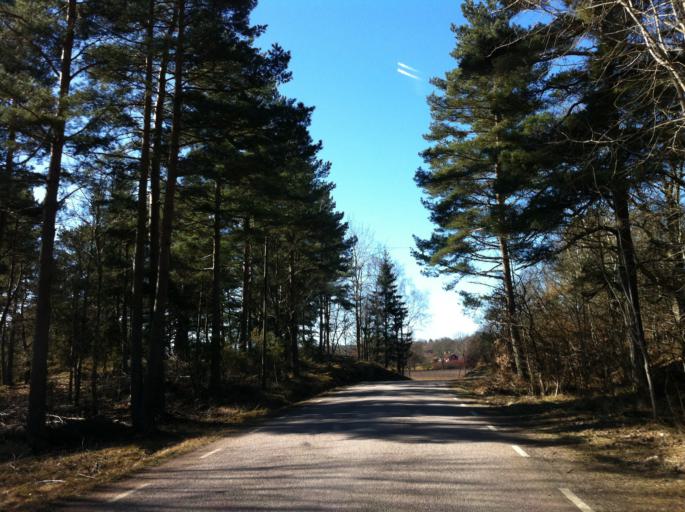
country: SE
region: Vaestra Goetaland
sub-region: Grastorps Kommun
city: Graestorp
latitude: 58.4365
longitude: 12.6085
